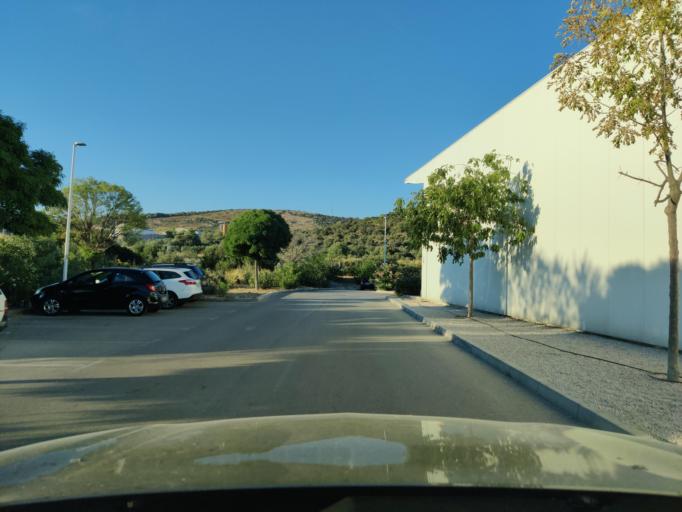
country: HR
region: Sibensko-Kniniska
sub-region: Grad Sibenik
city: Sibenik
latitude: 43.7561
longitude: 15.8776
